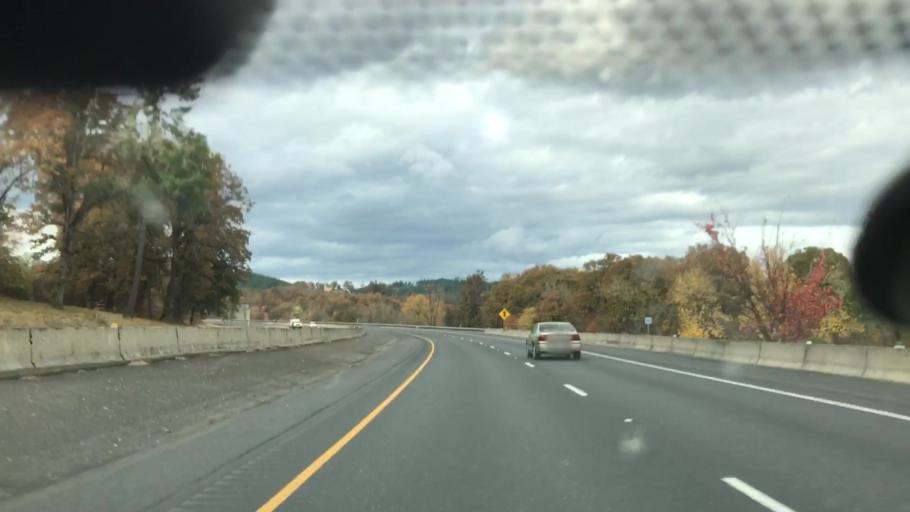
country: US
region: Oregon
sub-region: Douglas County
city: Sutherlin
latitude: 43.4692
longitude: -123.3160
